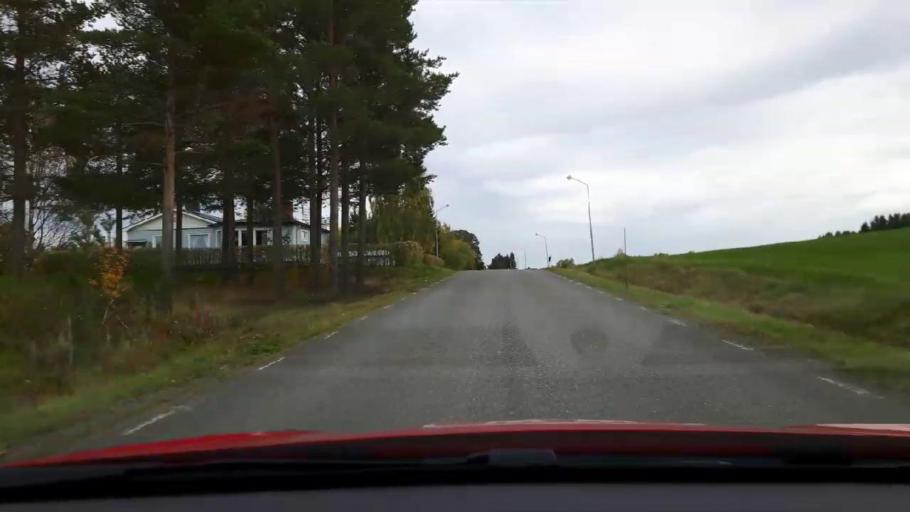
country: SE
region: Jaemtland
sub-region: Krokoms Kommun
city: Krokom
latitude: 63.2287
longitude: 14.1296
